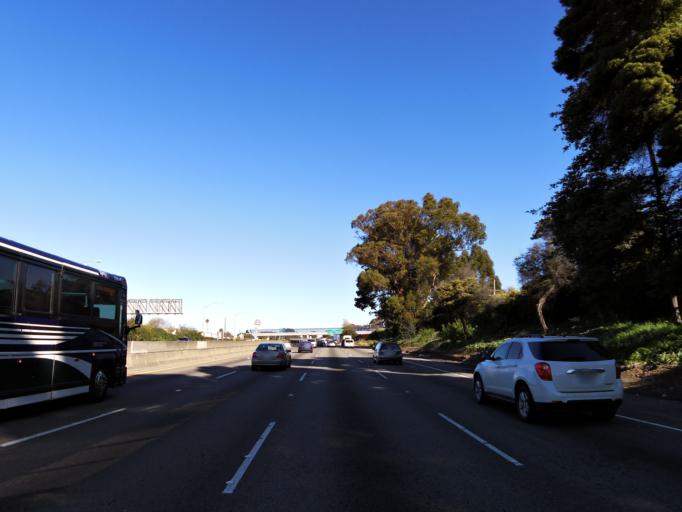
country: US
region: California
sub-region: Contra Costa County
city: East Richmond Heights
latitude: 37.9503
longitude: -122.3267
